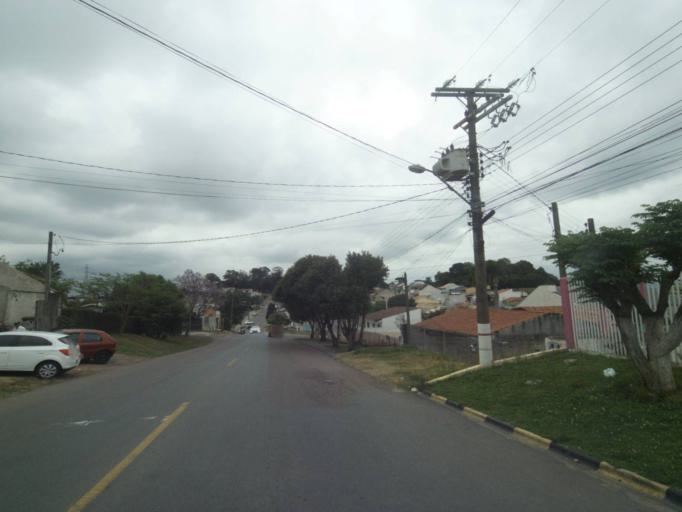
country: BR
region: Parana
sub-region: Sao Jose Dos Pinhais
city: Sao Jose dos Pinhais
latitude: -25.5451
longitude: -49.2880
